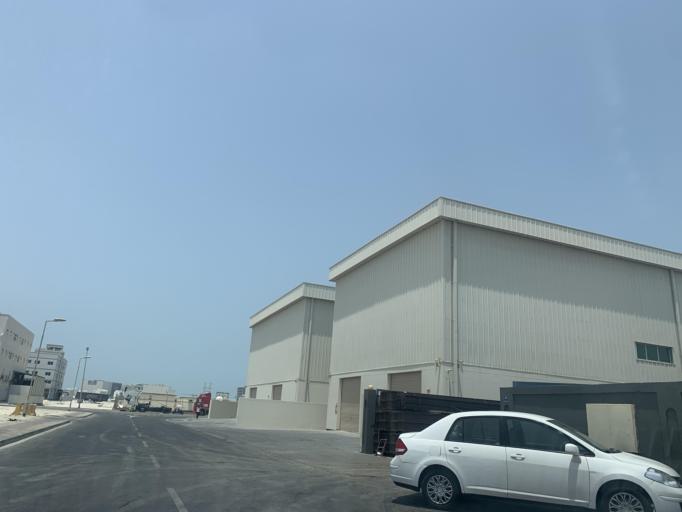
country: BH
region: Muharraq
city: Al Hadd
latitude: 26.2588
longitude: 50.6712
